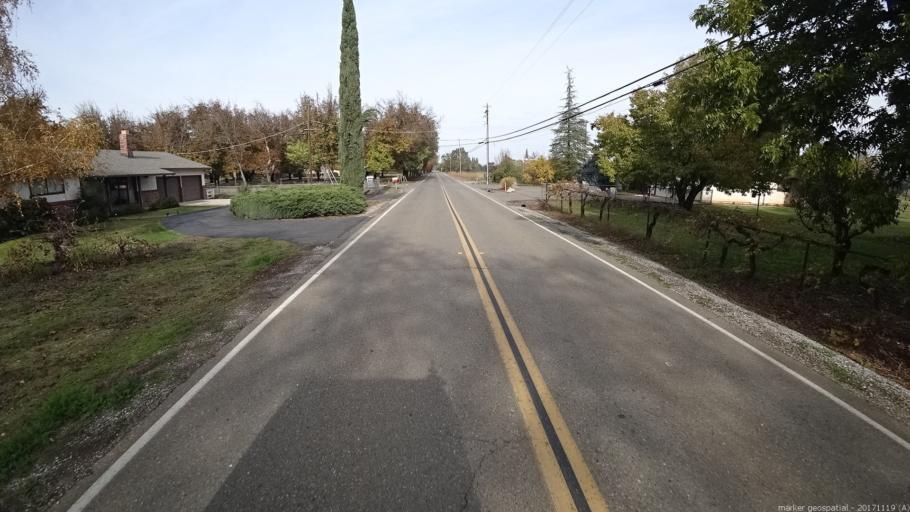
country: US
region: California
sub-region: Shasta County
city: Anderson
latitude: 40.4864
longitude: -122.3168
